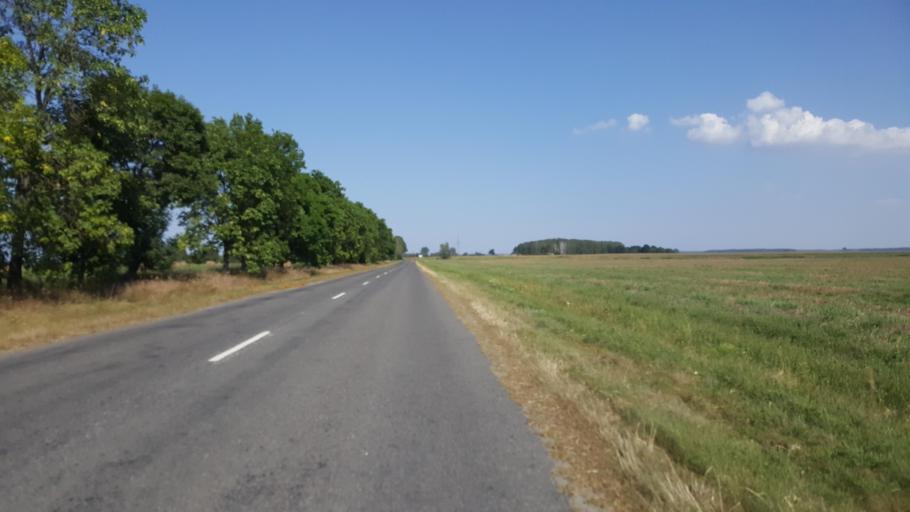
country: PL
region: Podlasie
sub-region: Powiat hajnowski
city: Czeremcha
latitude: 52.4841
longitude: 23.5413
